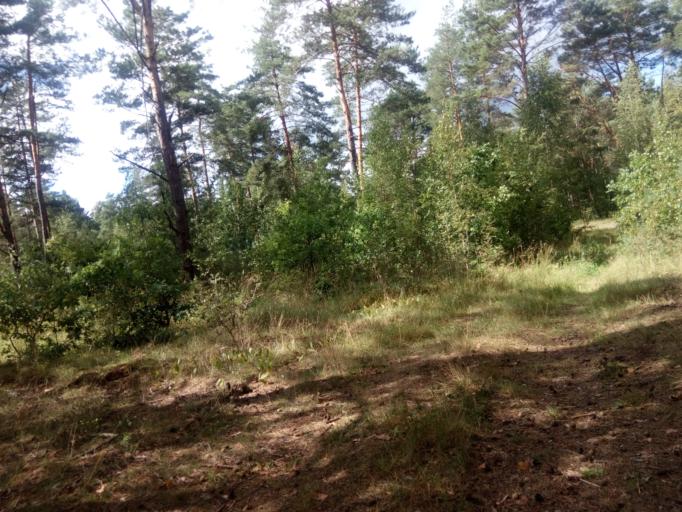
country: BY
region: Vitebsk
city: Dzisna
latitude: 55.6813
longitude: 28.2790
